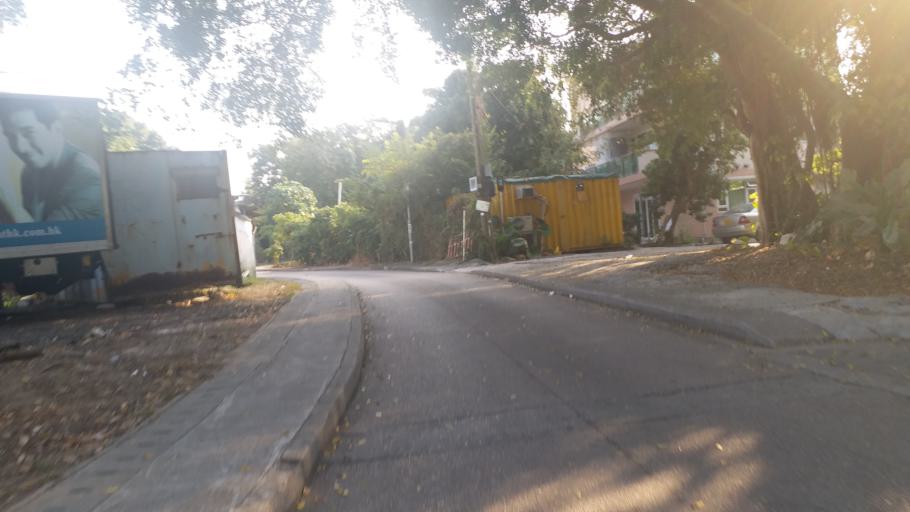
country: HK
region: Tuen Mun
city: Tuen Mun
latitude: 22.4170
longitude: 113.9738
